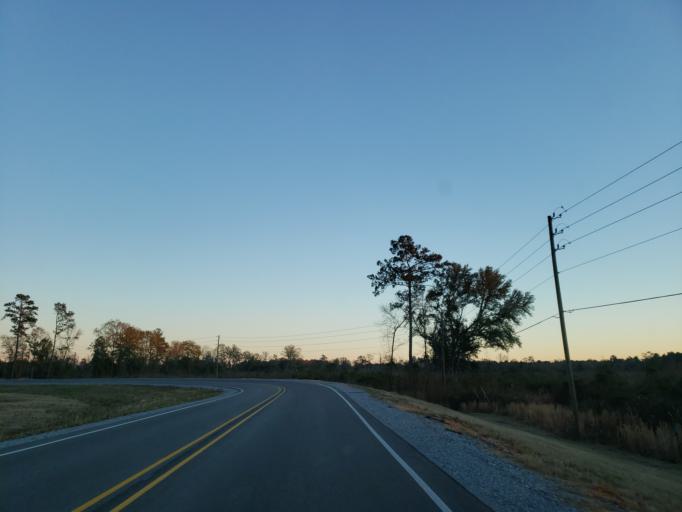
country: US
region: Mississippi
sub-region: Forrest County
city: Glendale
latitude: 31.3767
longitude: -89.3211
